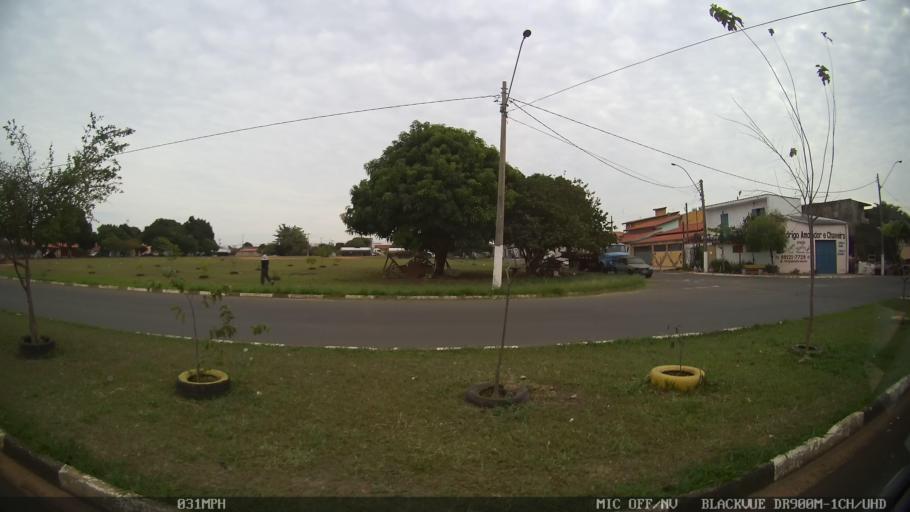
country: BR
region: Sao Paulo
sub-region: Paulinia
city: Paulinia
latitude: -22.7233
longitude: -47.1709
